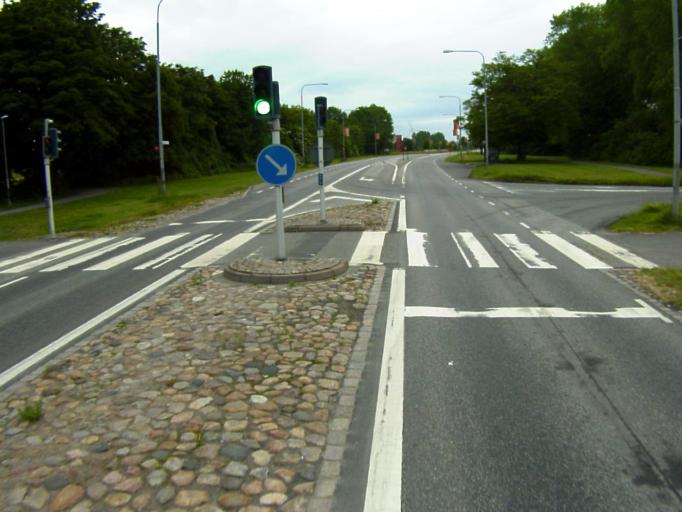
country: SE
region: Skane
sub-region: Kristianstads Kommun
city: Kristianstad
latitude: 56.0536
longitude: 14.1616
